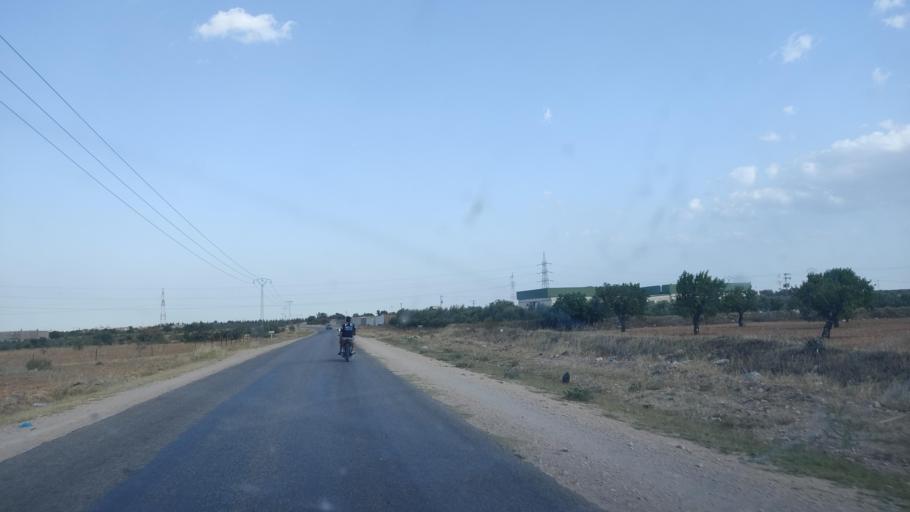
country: TN
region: Safaqis
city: Sfax
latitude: 34.8353
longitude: 10.6312
